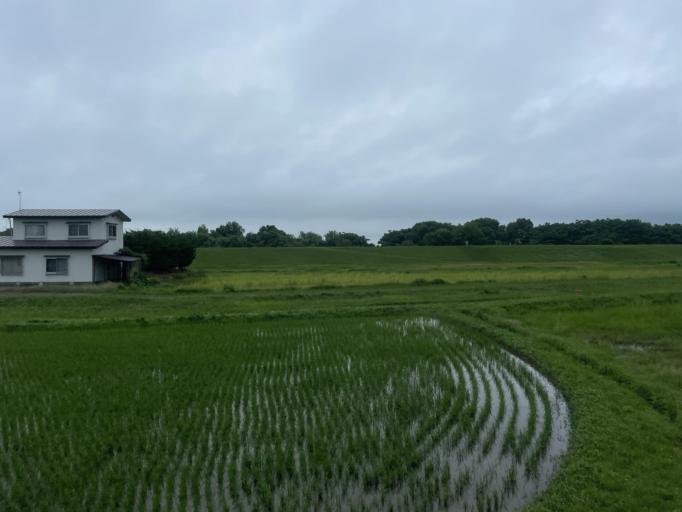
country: JP
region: Aomori
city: Goshogawara
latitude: 40.7882
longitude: 140.4400
